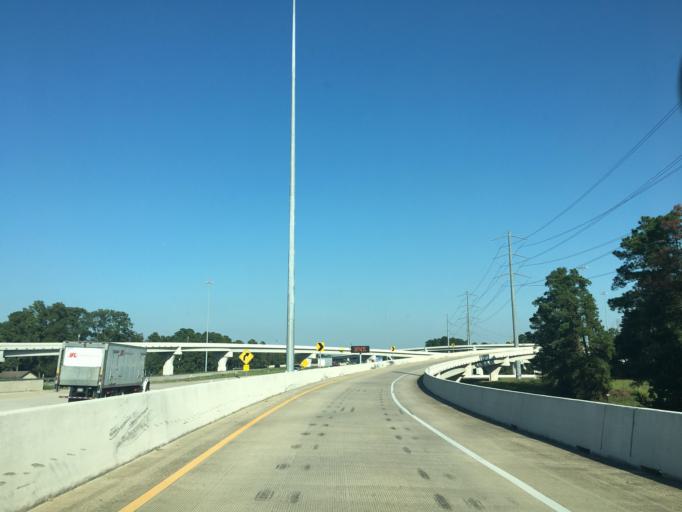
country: US
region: Texas
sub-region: Harris County
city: Spring
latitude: 30.0929
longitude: -95.4176
